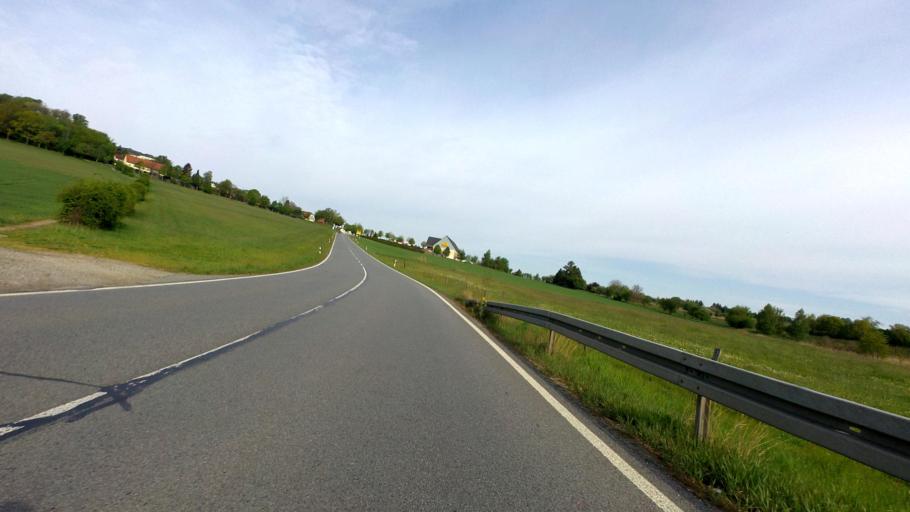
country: DE
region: Saxony
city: Stolpen
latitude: 51.0486
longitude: 14.0932
